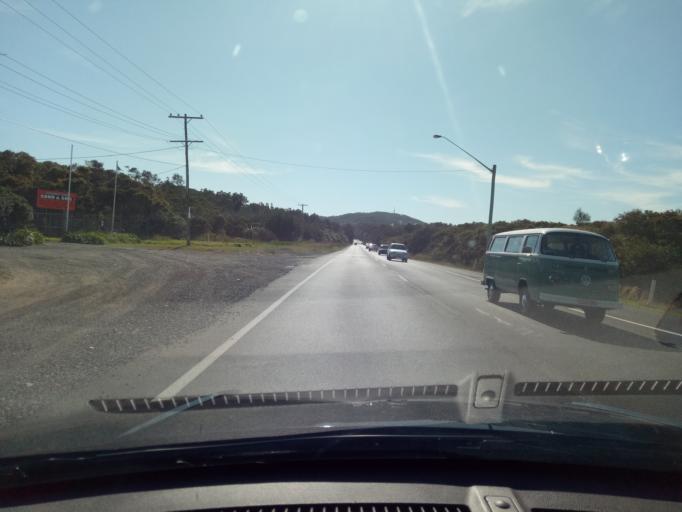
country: AU
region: New South Wales
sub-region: Gosford Shire
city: Forresters Beach
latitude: -33.4127
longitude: 151.4540
